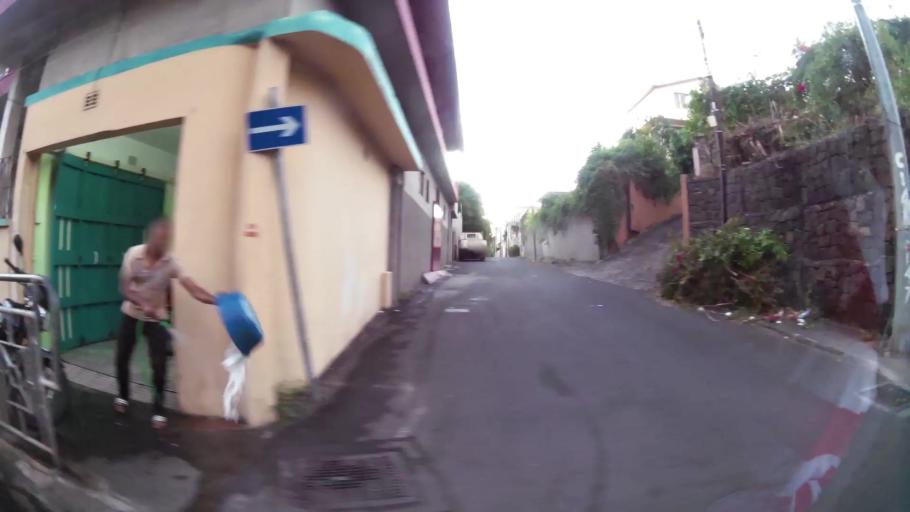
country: MU
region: Port Louis
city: Port Louis
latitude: -20.1686
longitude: 57.5142
